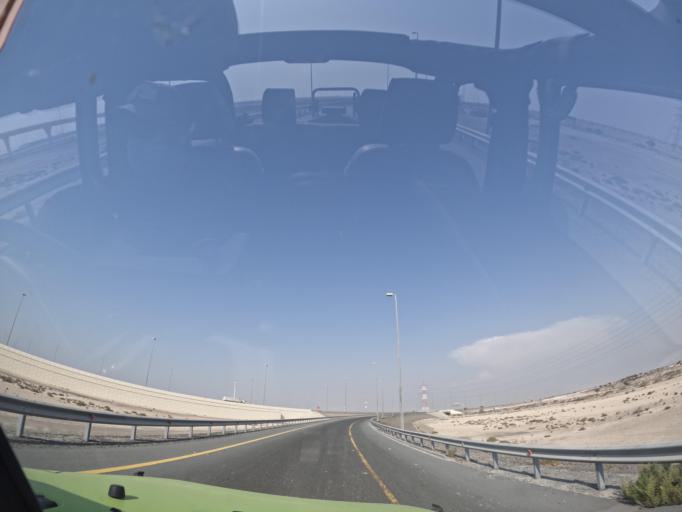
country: AE
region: Abu Dhabi
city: Abu Dhabi
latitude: 24.6771
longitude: 54.8243
